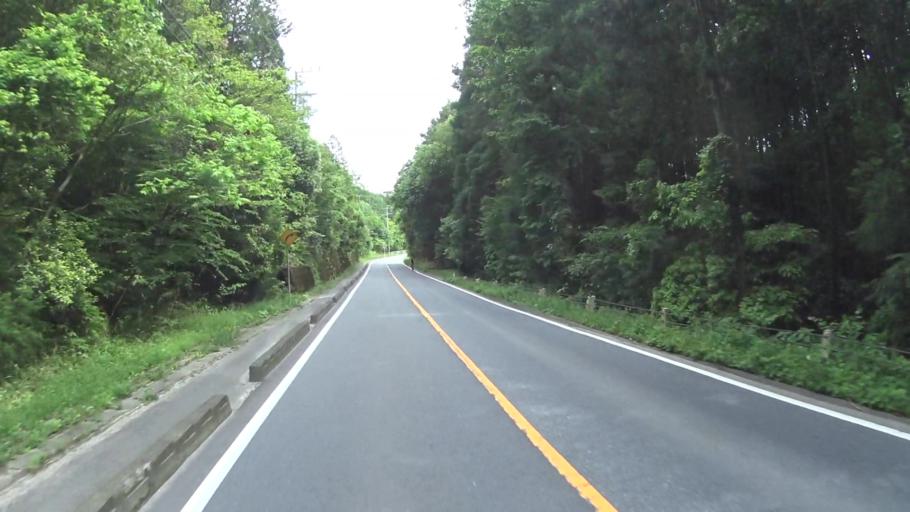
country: JP
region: Shiga Prefecture
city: Kitahama
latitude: 35.1446
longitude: 135.8795
